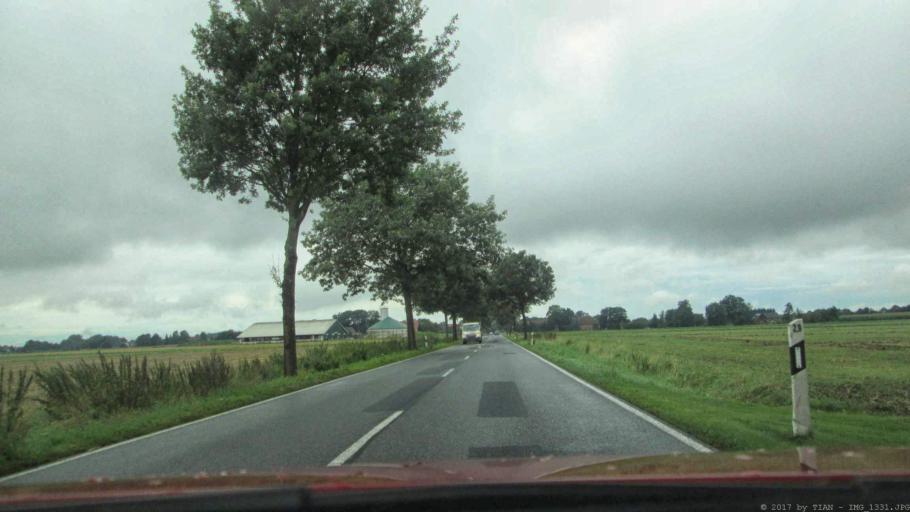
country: DE
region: Lower Saxony
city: Wittingen
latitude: 52.7061
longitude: 10.7772
